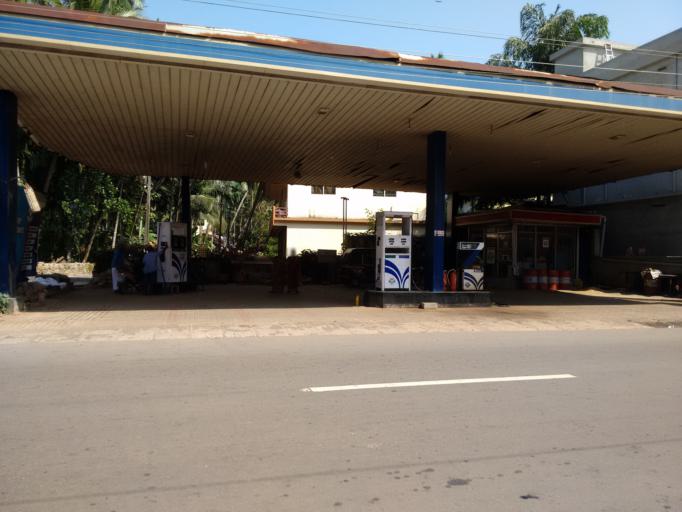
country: IN
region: Kerala
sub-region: Kozhikode
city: Badagara
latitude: 11.6018
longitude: 75.5851
